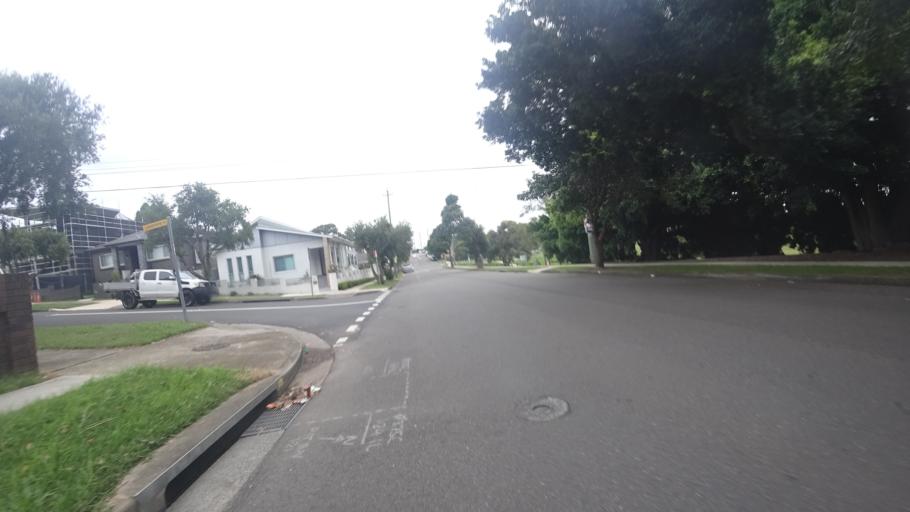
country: AU
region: New South Wales
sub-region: Rockdale
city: Bardwell Valley
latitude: -33.9403
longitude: 151.1303
